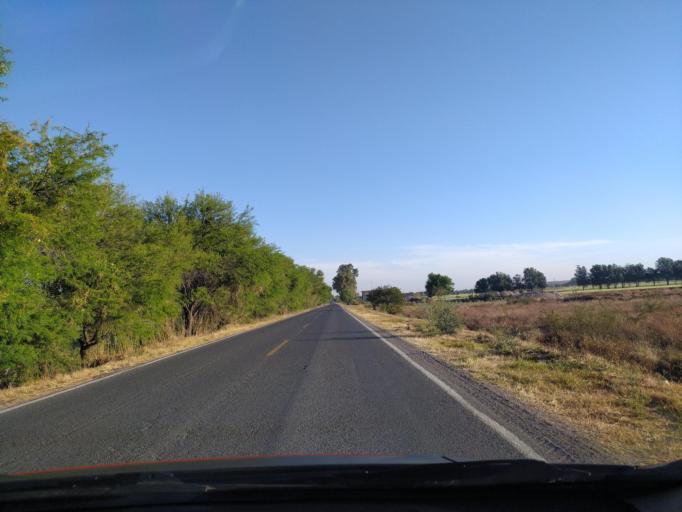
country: MX
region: Guanajuato
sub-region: San Francisco del Rincon
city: San Ignacio de Hidalgo
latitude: 20.9035
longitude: -101.8576
